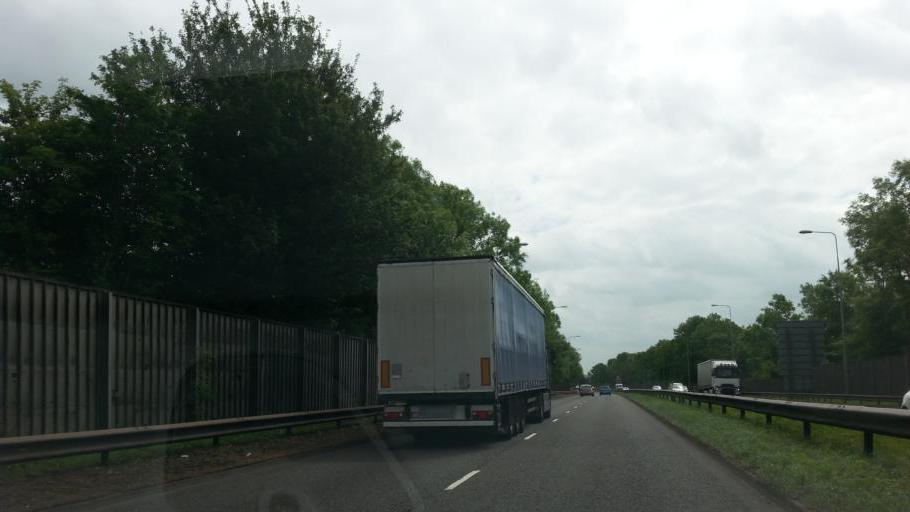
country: GB
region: England
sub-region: Staffordshire
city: Longton
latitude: 52.9638
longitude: -2.0705
